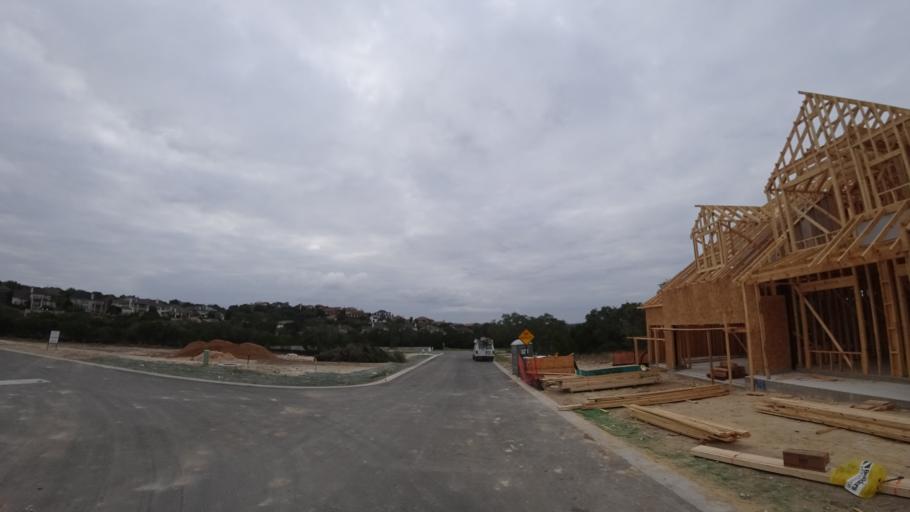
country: US
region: Texas
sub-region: Travis County
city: Bee Cave
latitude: 30.3177
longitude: -97.9127
